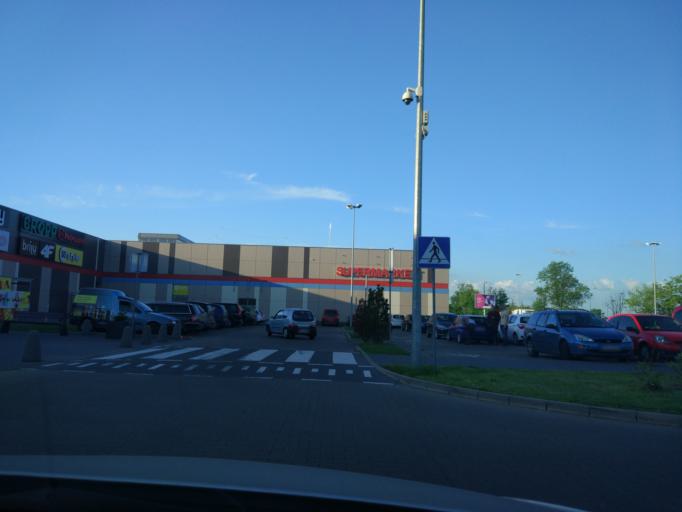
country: PL
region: Lodz Voivodeship
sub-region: Powiat kutnowski
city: Kutno
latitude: 52.2443
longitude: 19.3753
